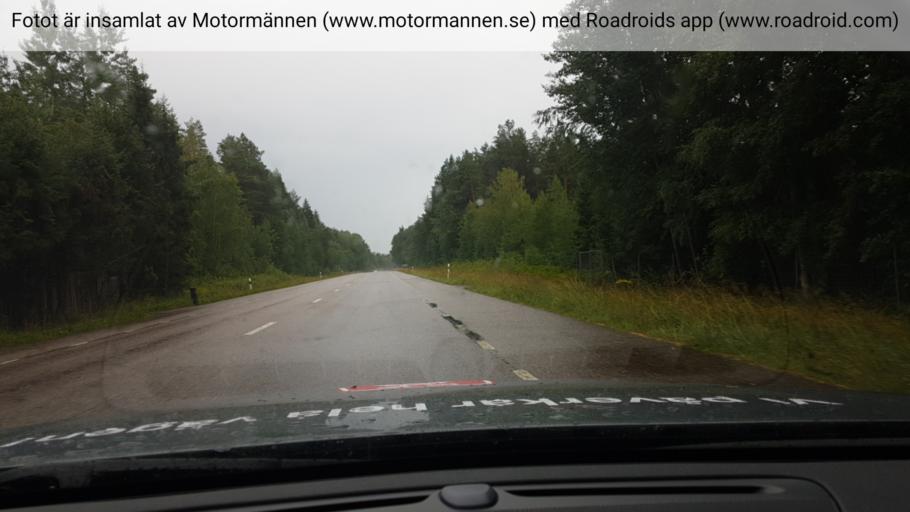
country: SE
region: Uppsala
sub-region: Alvkarleby Kommun
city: AElvkarleby
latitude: 60.5918
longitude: 17.4632
